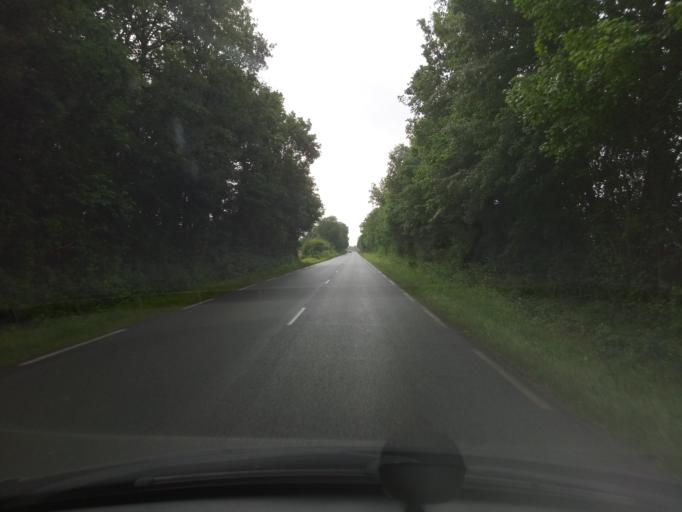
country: FR
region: Poitou-Charentes
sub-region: Departement de la Charente-Maritime
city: Courcon
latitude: 46.1803
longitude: -0.8513
